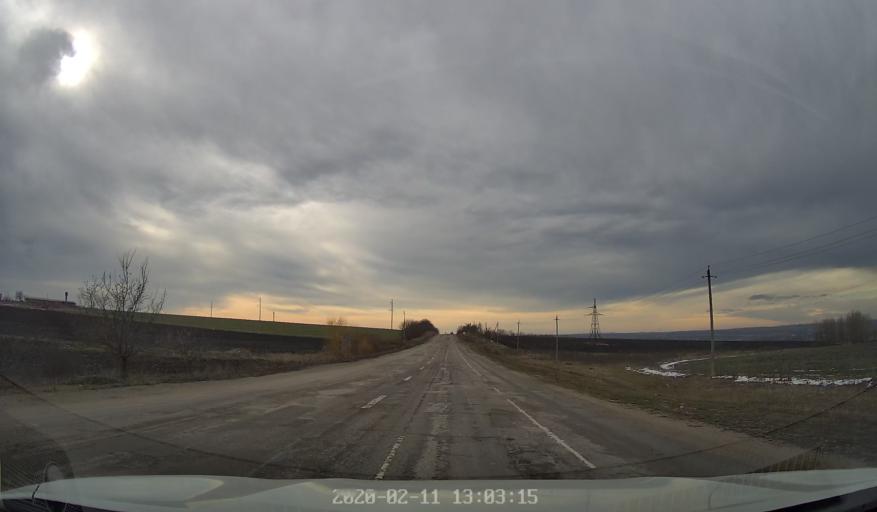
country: MD
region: Briceni
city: Briceni
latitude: 48.3137
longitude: 26.9635
